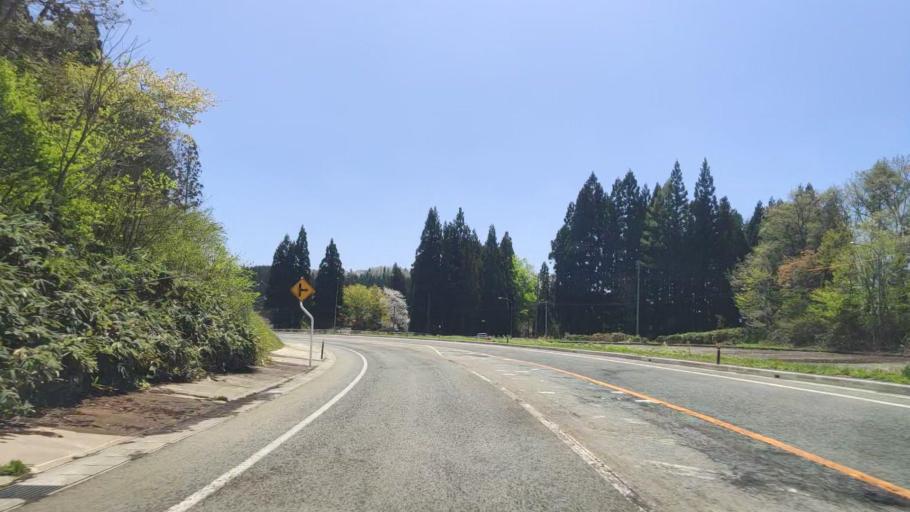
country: JP
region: Yamagata
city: Shinjo
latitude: 38.8921
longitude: 140.3235
